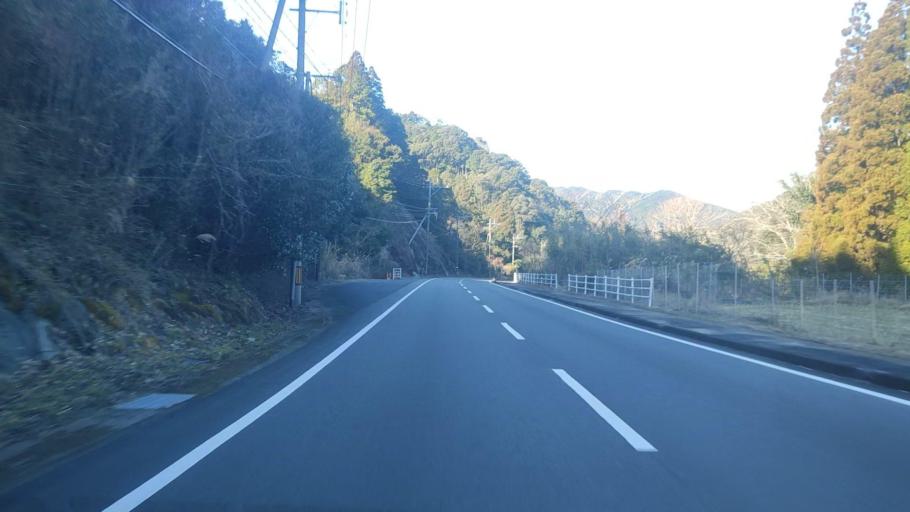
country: JP
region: Oita
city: Saiki
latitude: 32.7442
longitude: 131.8203
